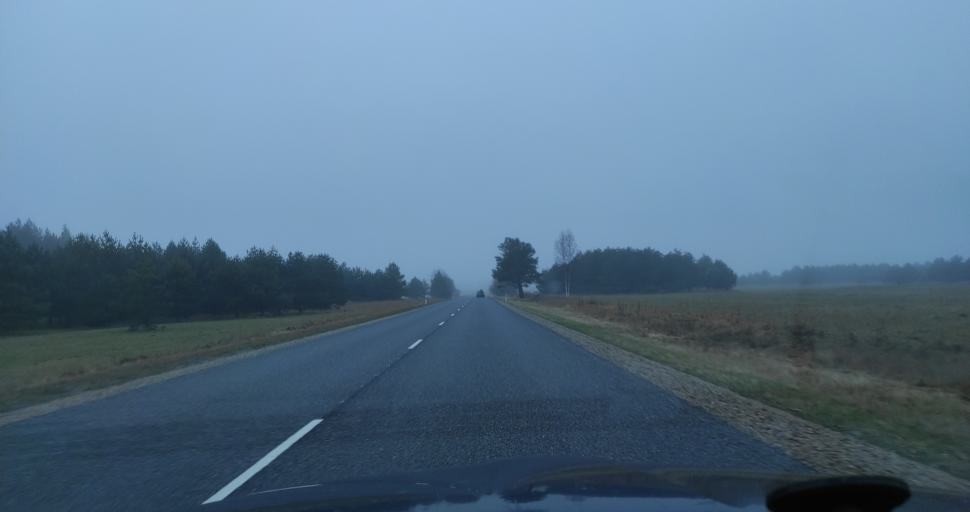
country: LV
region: Pavilostas
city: Pavilosta
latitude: 56.9566
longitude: 21.3209
